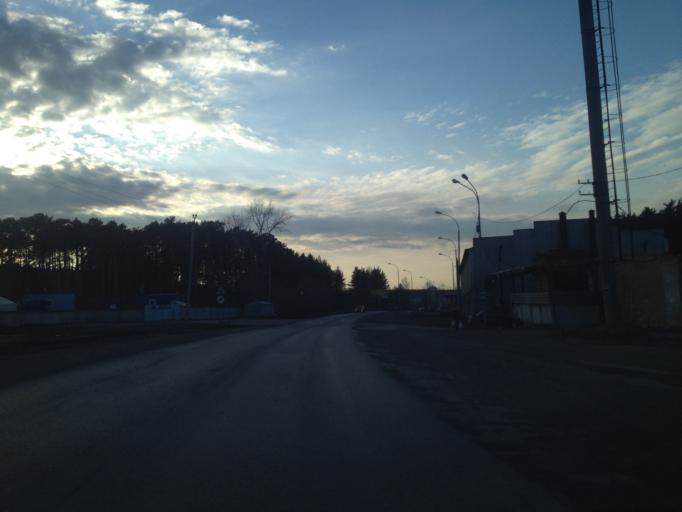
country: RU
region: Sverdlovsk
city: Shirokaya Rechka
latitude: 56.8175
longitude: 60.5138
